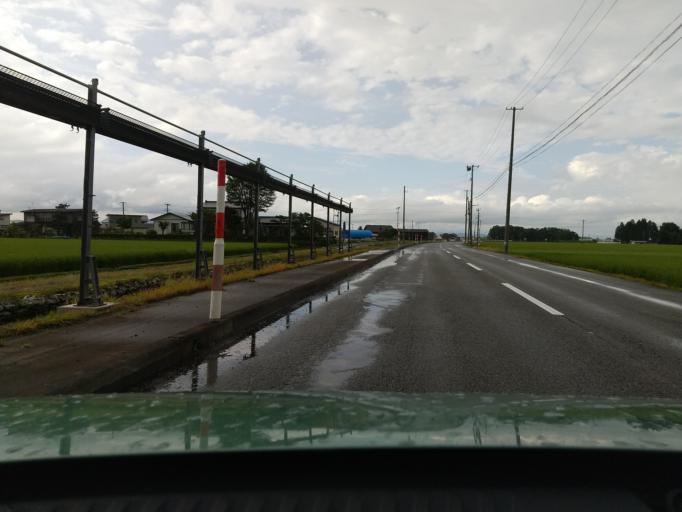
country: JP
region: Akita
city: Omagari
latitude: 39.3708
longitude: 140.4715
